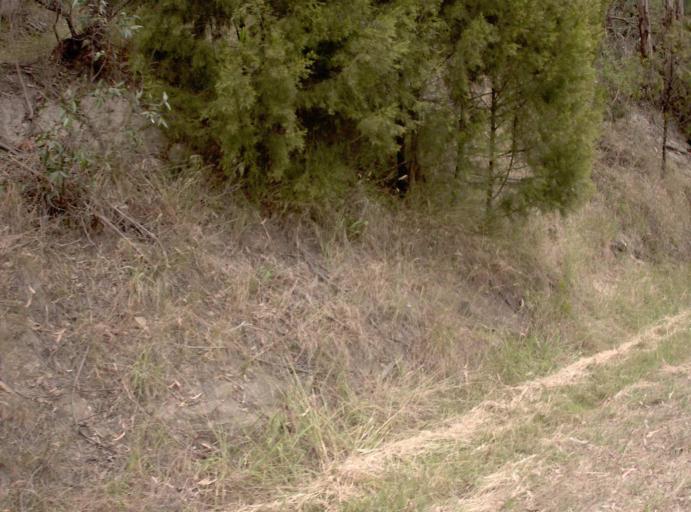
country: AU
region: Victoria
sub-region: Latrobe
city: Traralgon
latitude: -38.4879
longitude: 146.6383
